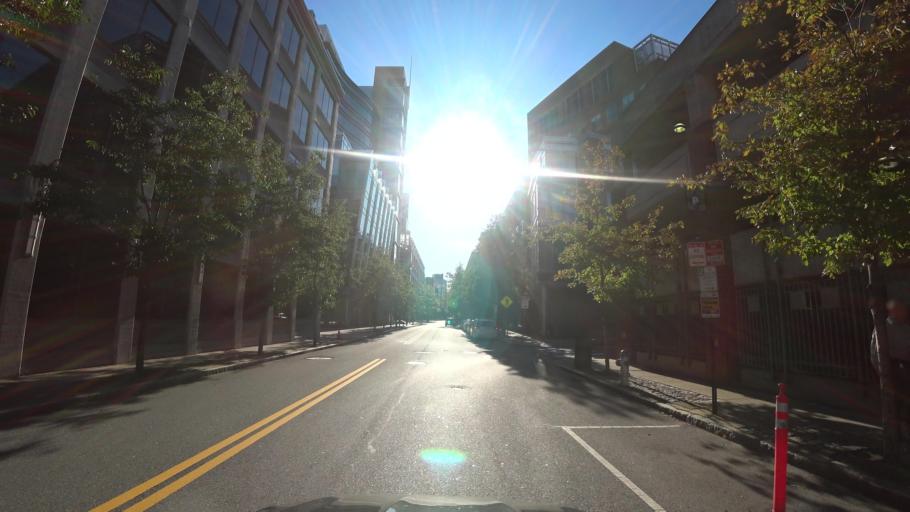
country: US
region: Massachusetts
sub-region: Middlesex County
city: Cambridge
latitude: 42.3612
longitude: -71.0989
